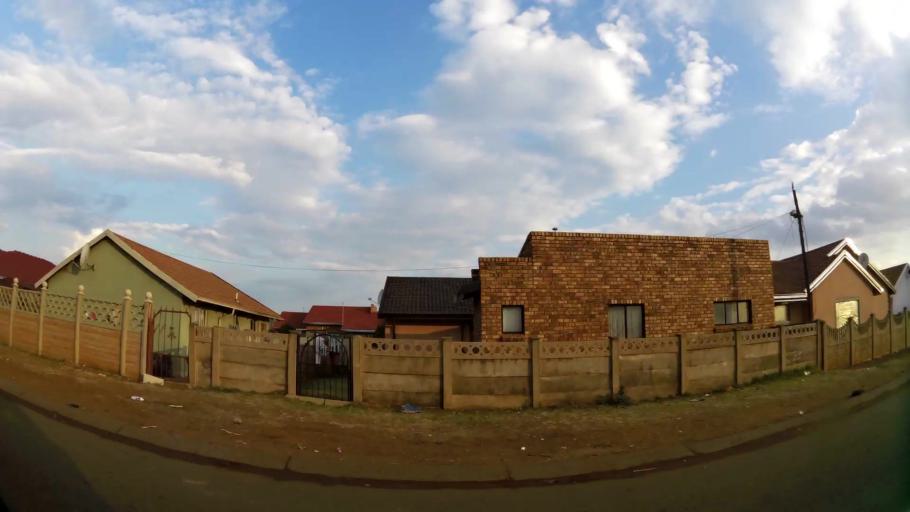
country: ZA
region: Gauteng
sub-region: City of Johannesburg Metropolitan Municipality
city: Orange Farm
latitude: -26.5937
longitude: 27.8337
